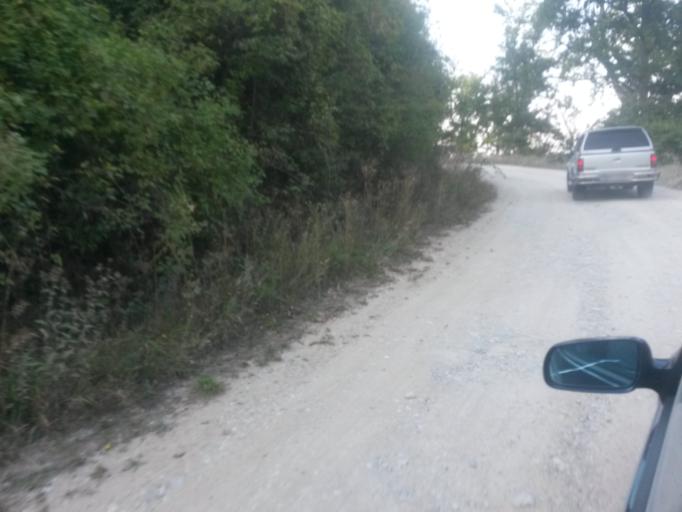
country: RO
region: Alba
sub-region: Comuna Livezile
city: Livezile
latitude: 46.3218
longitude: 23.6016
